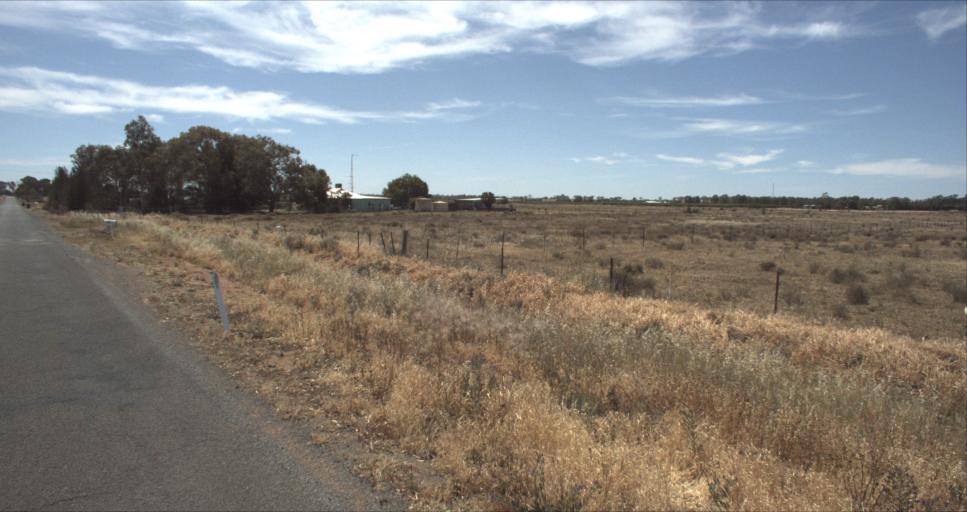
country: AU
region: New South Wales
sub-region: Leeton
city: Leeton
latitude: -34.6015
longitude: 146.4269
